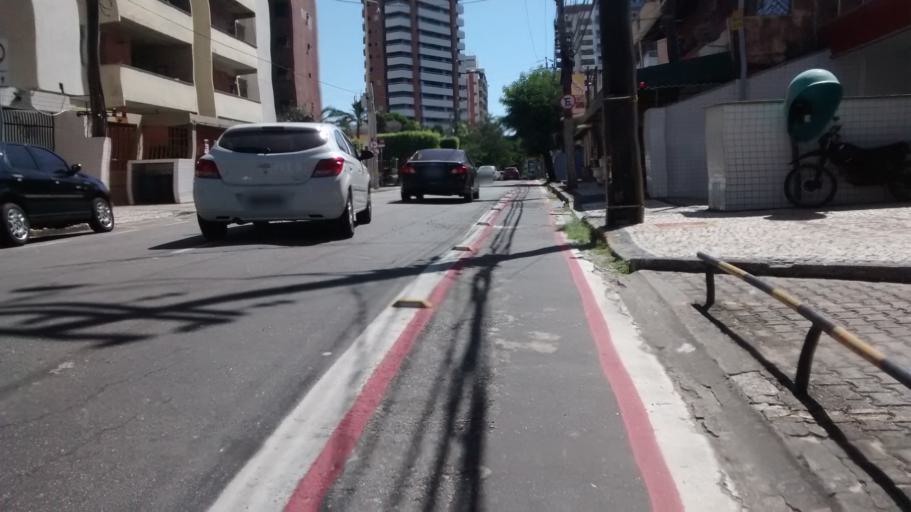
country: BR
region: Ceara
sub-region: Fortaleza
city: Fortaleza
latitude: -3.7429
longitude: -38.5011
